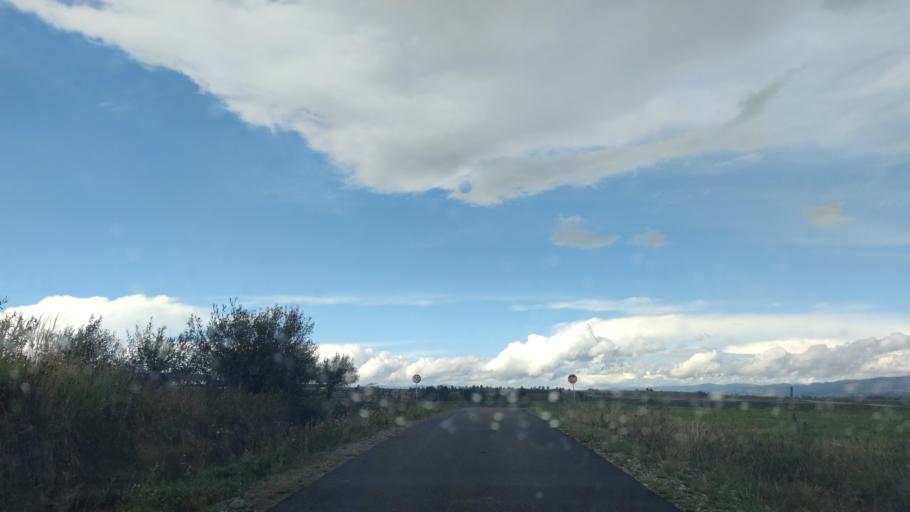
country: RO
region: Harghita
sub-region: Comuna Remetea
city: Remetea
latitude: 46.8151
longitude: 25.3826
